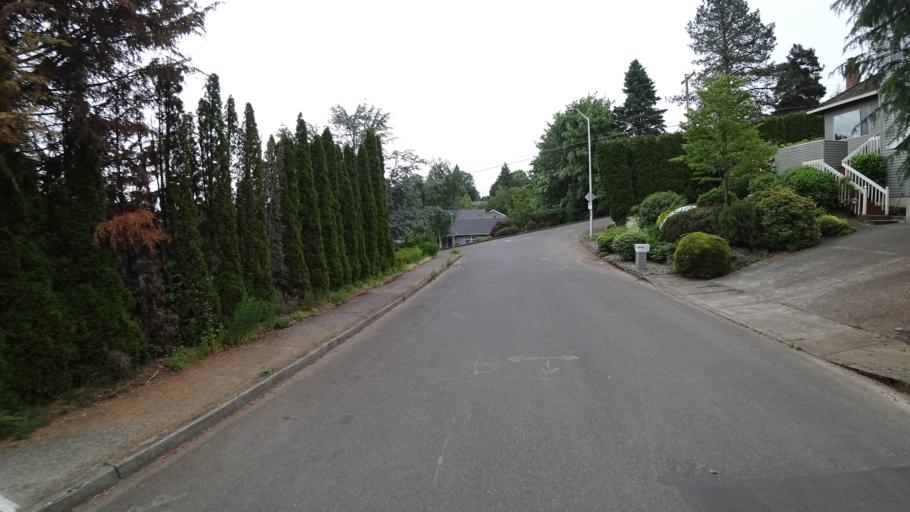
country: US
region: Oregon
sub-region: Clackamas County
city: Lake Oswego
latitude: 45.4385
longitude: -122.7068
